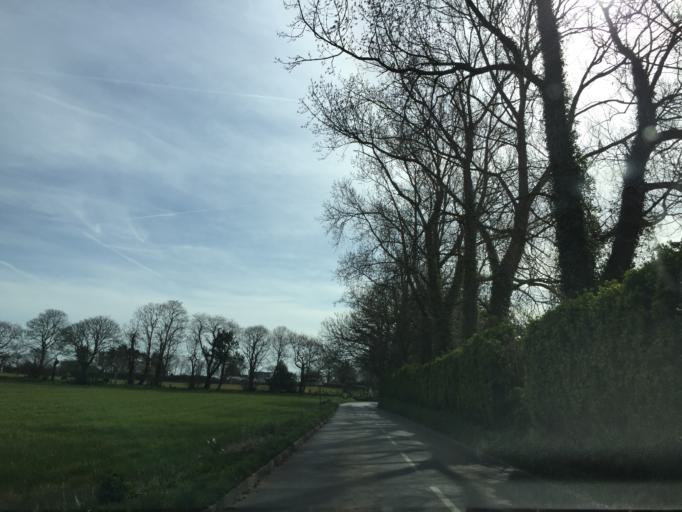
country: JE
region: St Helier
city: Saint Helier
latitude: 49.2289
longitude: -2.0709
